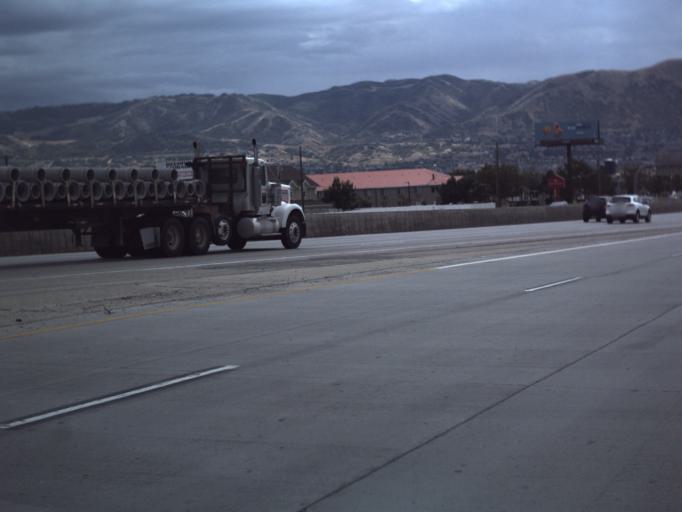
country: US
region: Utah
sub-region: Salt Lake County
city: Draper
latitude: 40.5242
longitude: -111.8916
